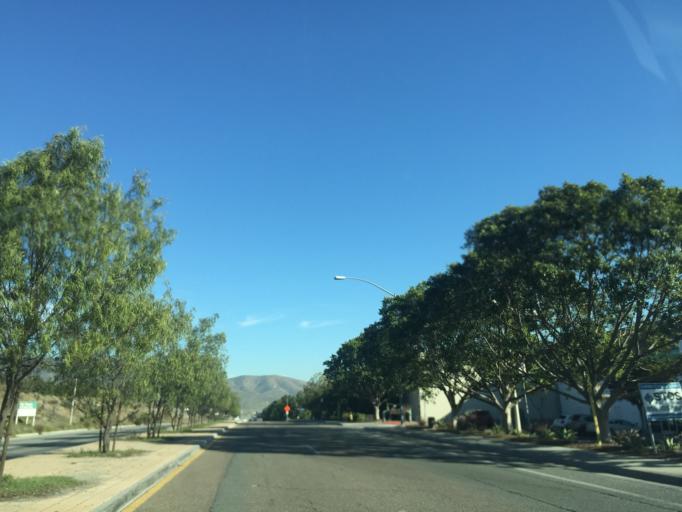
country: MX
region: Baja California
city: Tijuana
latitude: 32.5601
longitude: -116.9338
